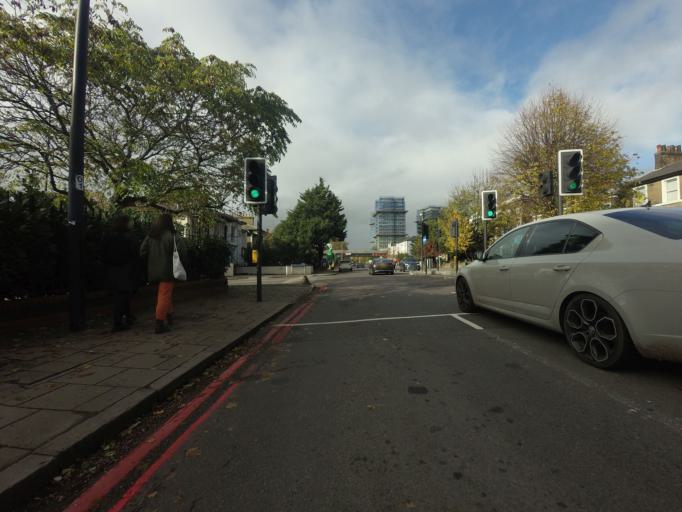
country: GB
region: England
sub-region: Greater London
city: Camberwell
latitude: 51.4778
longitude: -0.0524
